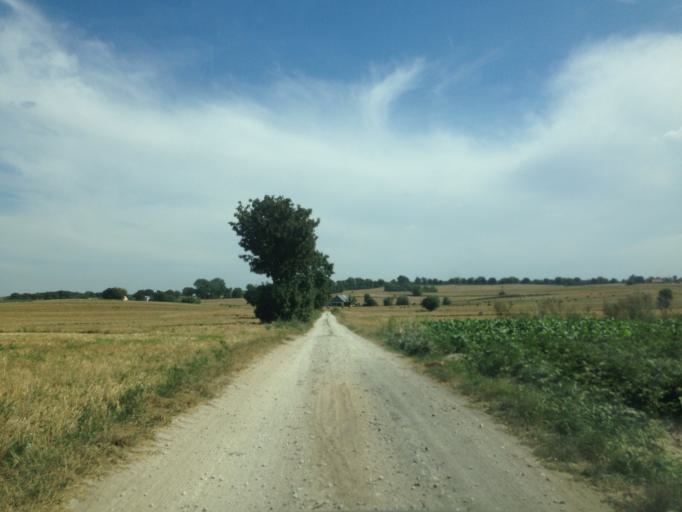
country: PL
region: Kujawsko-Pomorskie
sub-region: Powiat brodnicki
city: Bartniczka
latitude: 53.2267
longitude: 19.6183
